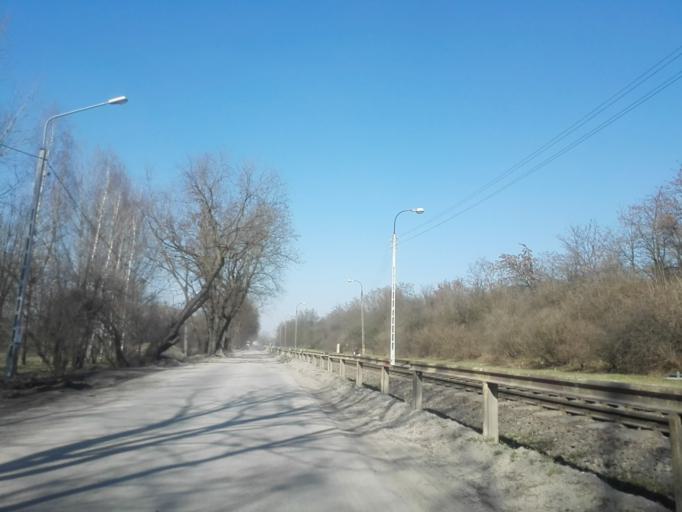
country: PL
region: Masovian Voivodeship
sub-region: Warszawa
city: Wilanow
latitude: 52.1481
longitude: 21.1434
